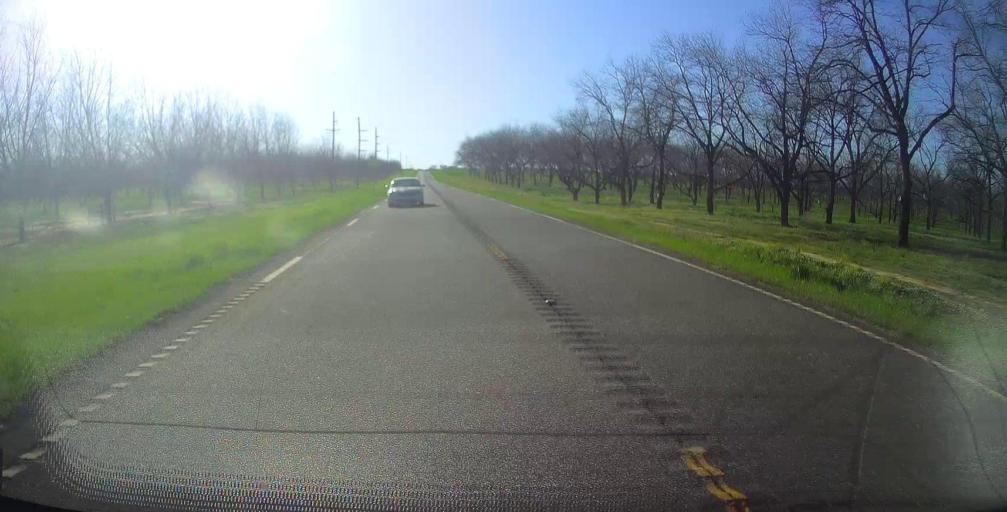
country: US
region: Georgia
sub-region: Macon County
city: Marshallville
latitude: 32.4395
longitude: -83.8666
